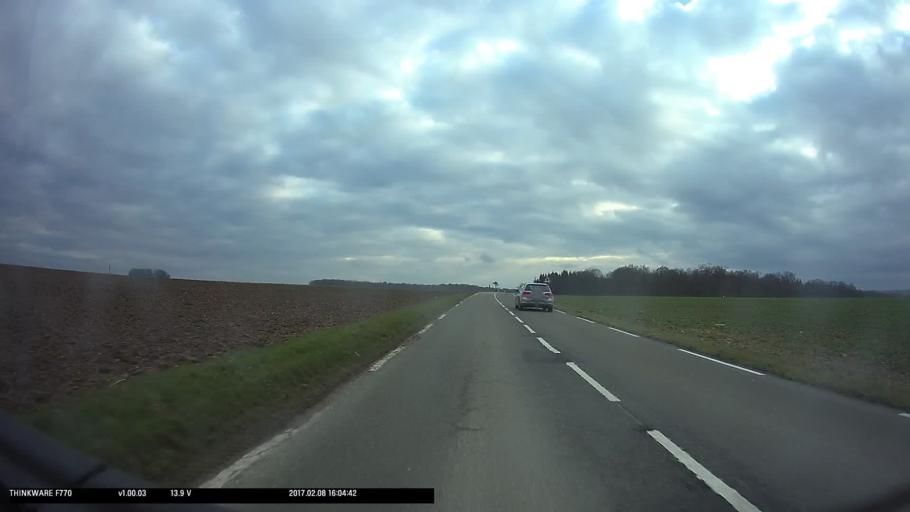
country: FR
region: Ile-de-France
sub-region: Departement du Val-d'Oise
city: Us
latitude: 49.1187
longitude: 1.9818
